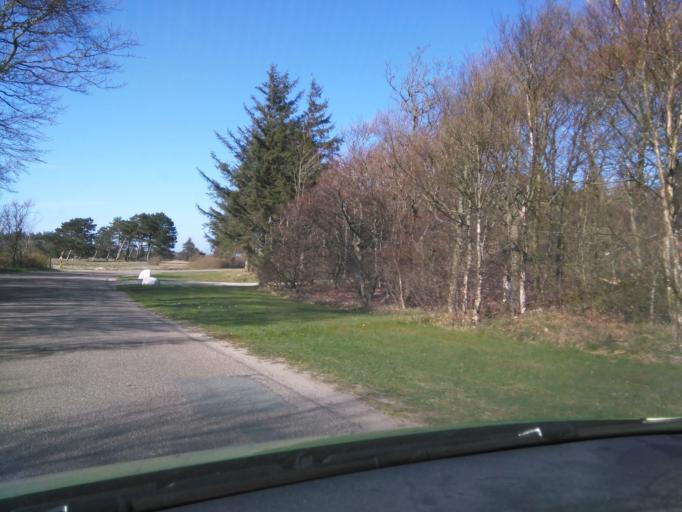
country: DK
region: South Denmark
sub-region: Varde Kommune
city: Oksbol
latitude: 55.6828
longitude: 8.1861
